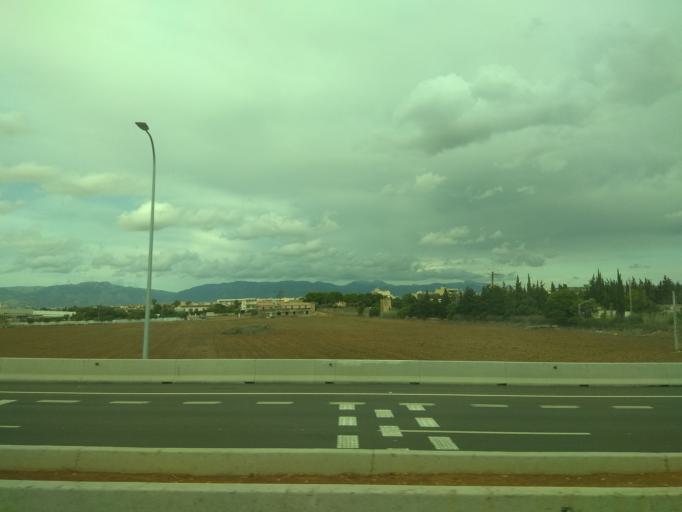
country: ES
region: Balearic Islands
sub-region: Illes Balears
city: Palma
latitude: 39.5681
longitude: 2.7121
